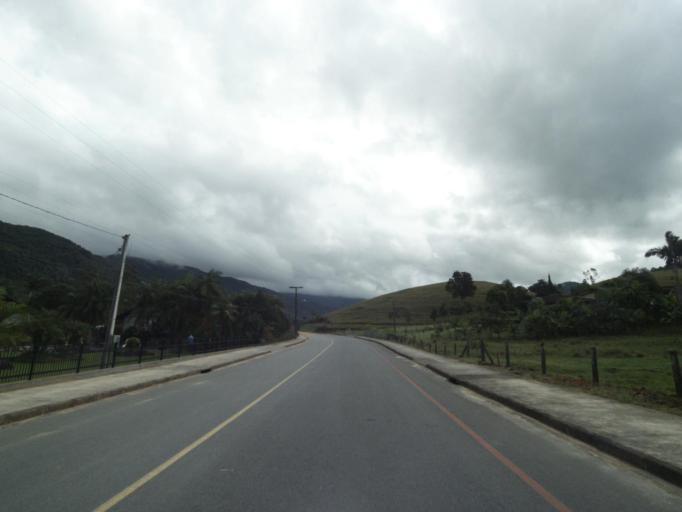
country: BR
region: Santa Catarina
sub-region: Pomerode
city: Pomerode
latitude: -26.6712
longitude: -49.1860
